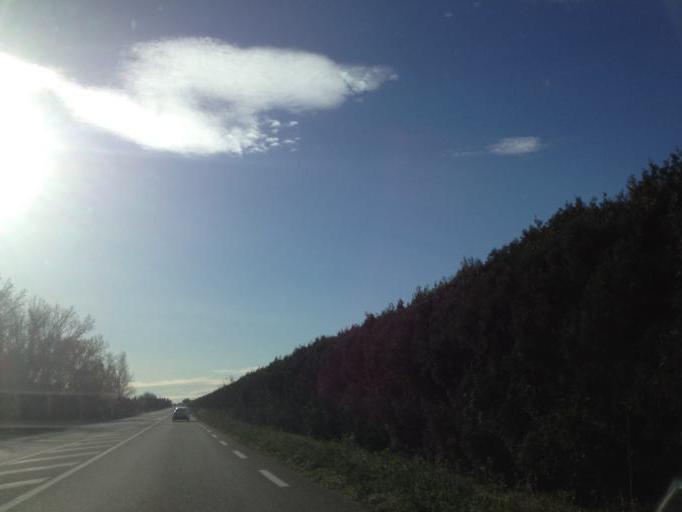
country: FR
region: Provence-Alpes-Cote d'Azur
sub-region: Departement du Vaucluse
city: Bedarrides
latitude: 44.0577
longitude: 4.8881
